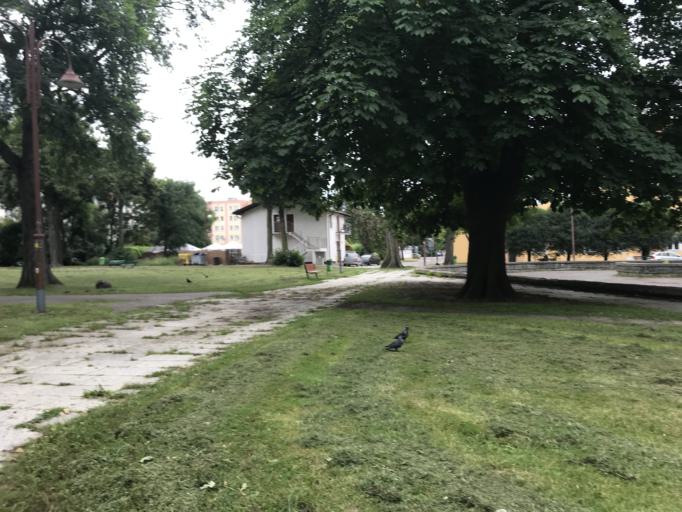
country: PL
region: Warmian-Masurian Voivodeship
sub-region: Powiat elblaski
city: Elblag
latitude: 54.1608
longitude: 19.4011
